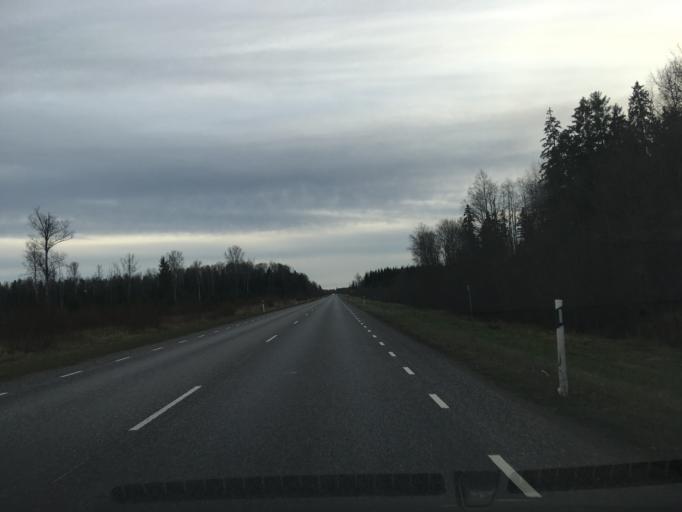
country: EE
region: Ida-Virumaa
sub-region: Johvi vald
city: Johvi
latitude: 59.3514
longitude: 27.4674
